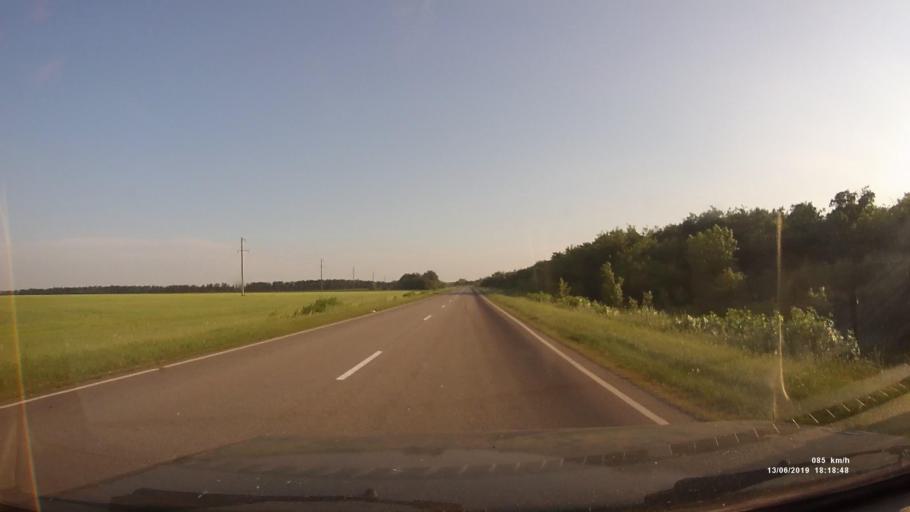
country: RU
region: Rostov
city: Kazanskaya
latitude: 49.9039
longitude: 41.3106
